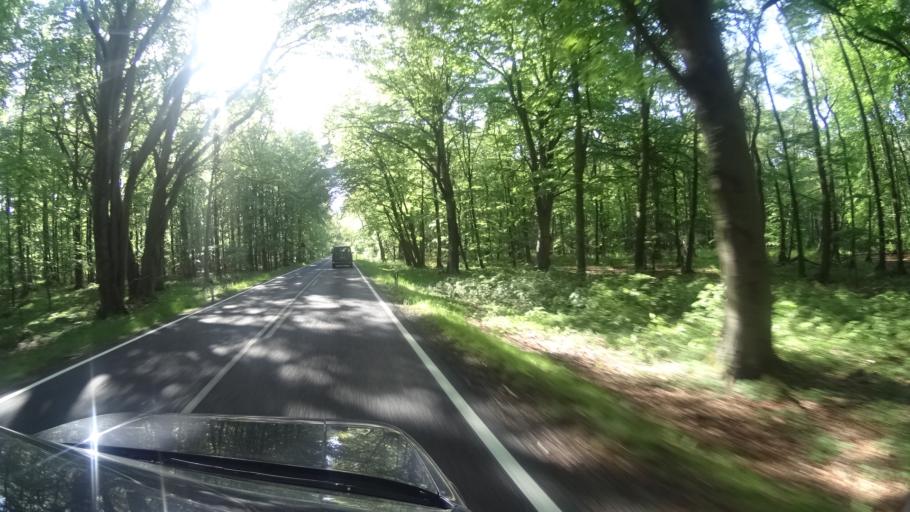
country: DE
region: Mecklenburg-Vorpommern
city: Born
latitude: 54.4017
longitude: 12.4830
